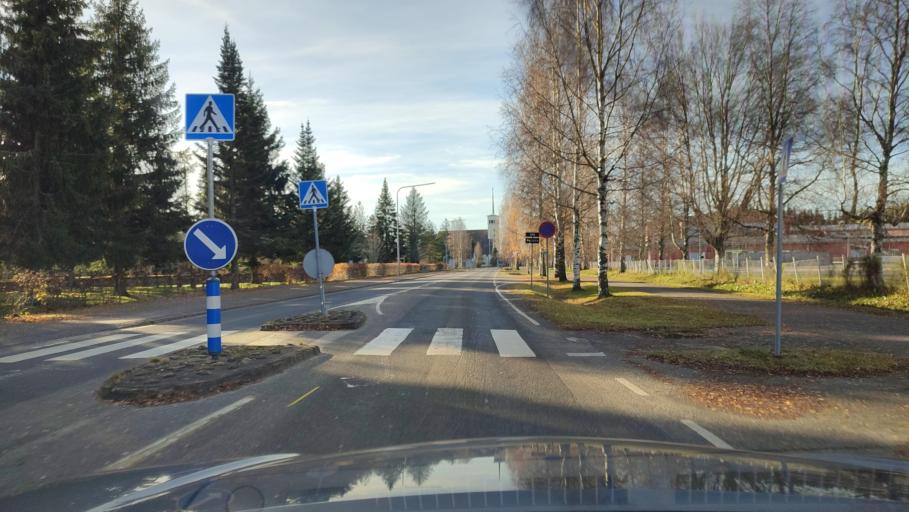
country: FI
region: Southern Ostrobothnia
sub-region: Suupohja
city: Teuva
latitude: 62.4815
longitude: 21.7430
